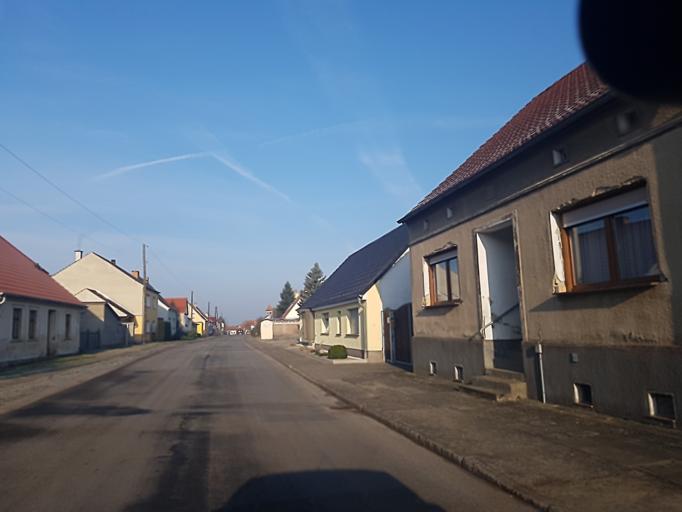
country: DE
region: Brandenburg
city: Wollin
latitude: 52.2467
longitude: 12.4887
